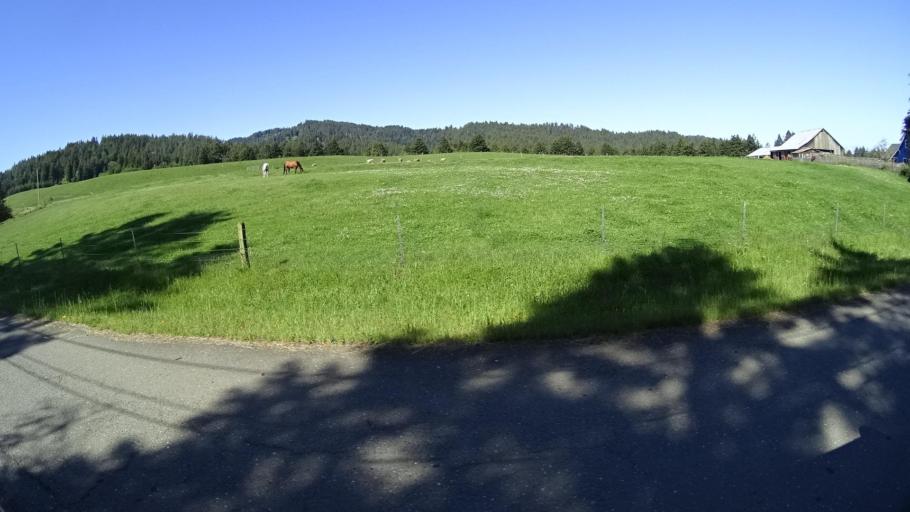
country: US
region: California
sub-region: Humboldt County
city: Rio Dell
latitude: 40.5188
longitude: -124.1633
